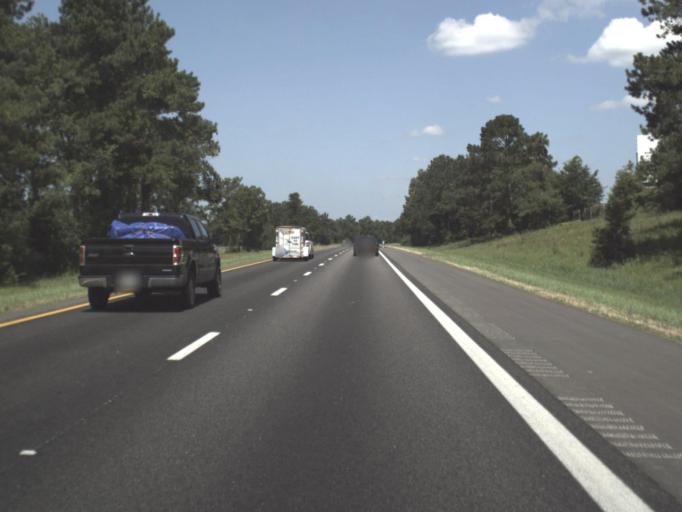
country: US
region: Florida
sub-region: Madison County
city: Madison
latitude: 30.4123
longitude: -83.4255
